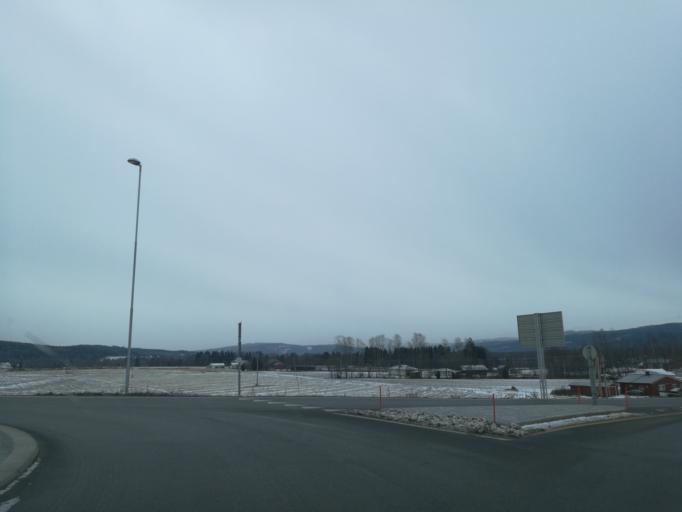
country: NO
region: Hedmark
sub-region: Kongsvinger
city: Spetalen
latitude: 60.2342
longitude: 11.8202
